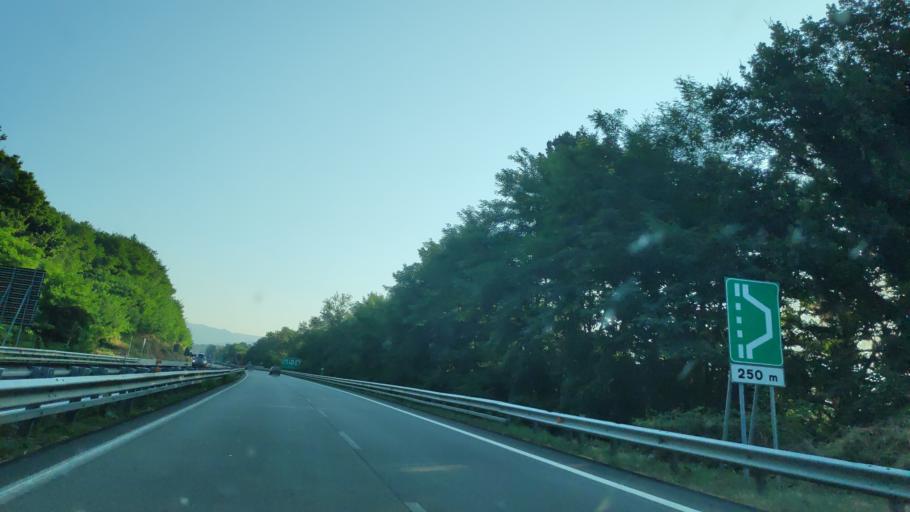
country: IT
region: Calabria
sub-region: Provincia di Cosenza
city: Marzi
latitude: 39.1817
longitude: 16.3022
